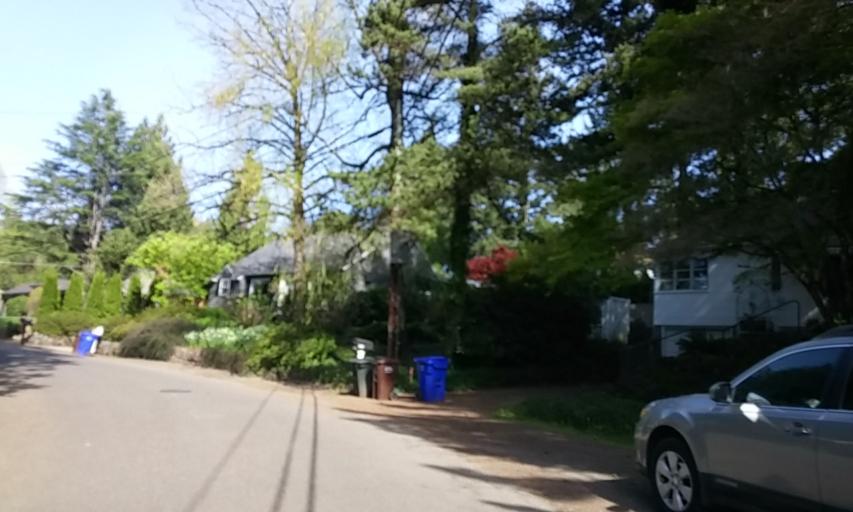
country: US
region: Oregon
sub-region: Washington County
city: West Slope
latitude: 45.5034
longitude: -122.7506
